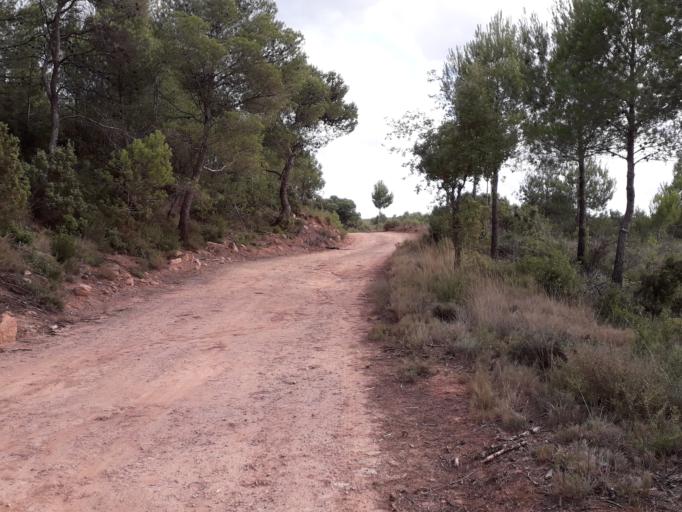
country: ES
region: Catalonia
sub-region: Provincia de Barcelona
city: Jorba
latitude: 41.6150
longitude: 1.4782
